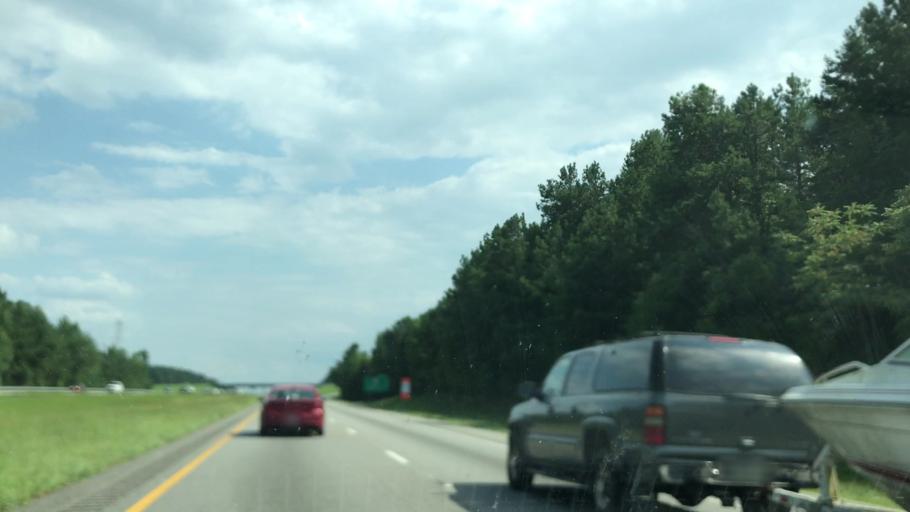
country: US
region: South Carolina
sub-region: Chester County
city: Great Falls
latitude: 34.6164
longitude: -81.0209
